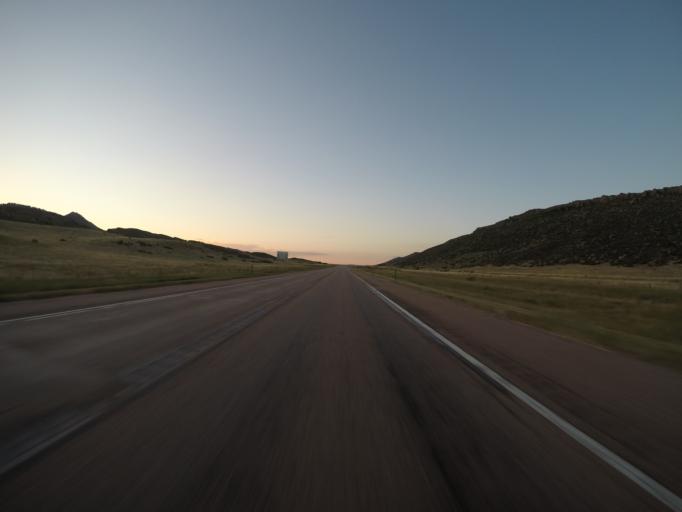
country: US
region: Colorado
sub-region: Larimer County
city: Laporte
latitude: 40.7157
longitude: -105.1723
